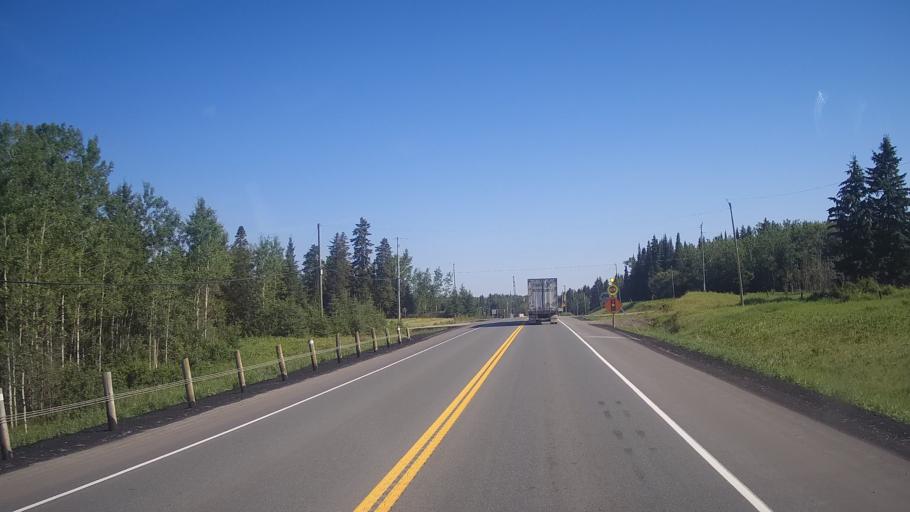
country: CA
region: Ontario
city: Dryden
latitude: 49.6818
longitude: -92.4927
